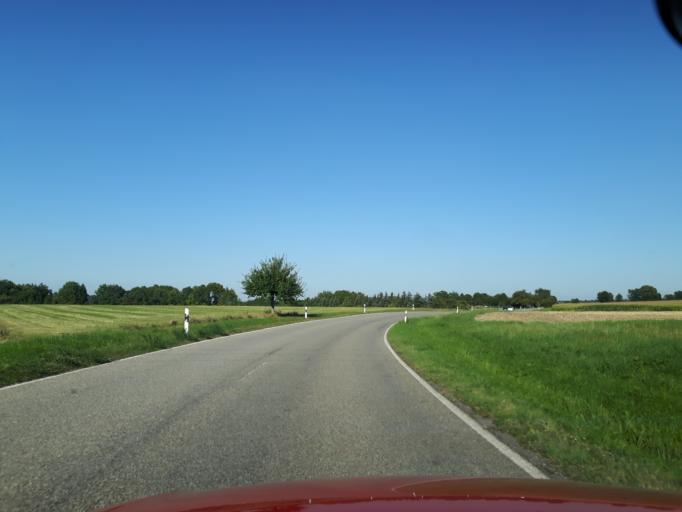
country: DE
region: Baden-Wuerttemberg
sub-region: Regierungsbezirk Stuttgart
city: Guglingen
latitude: 49.0508
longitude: 9.0056
